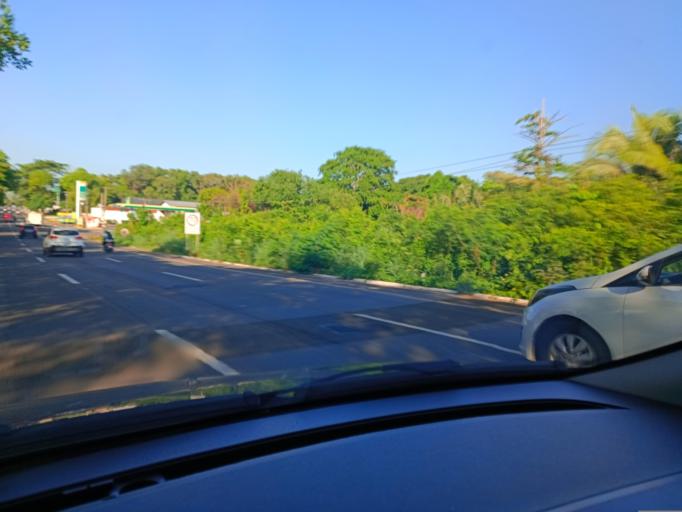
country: BR
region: Piaui
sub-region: Teresina
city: Teresina
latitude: -5.0799
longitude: -42.7557
